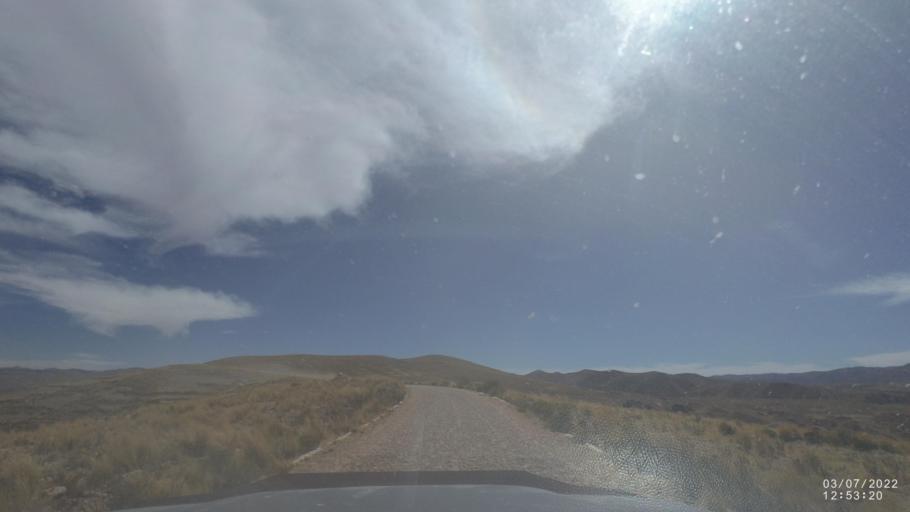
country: BO
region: Cochabamba
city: Irpa Irpa
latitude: -17.7451
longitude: -66.6624
